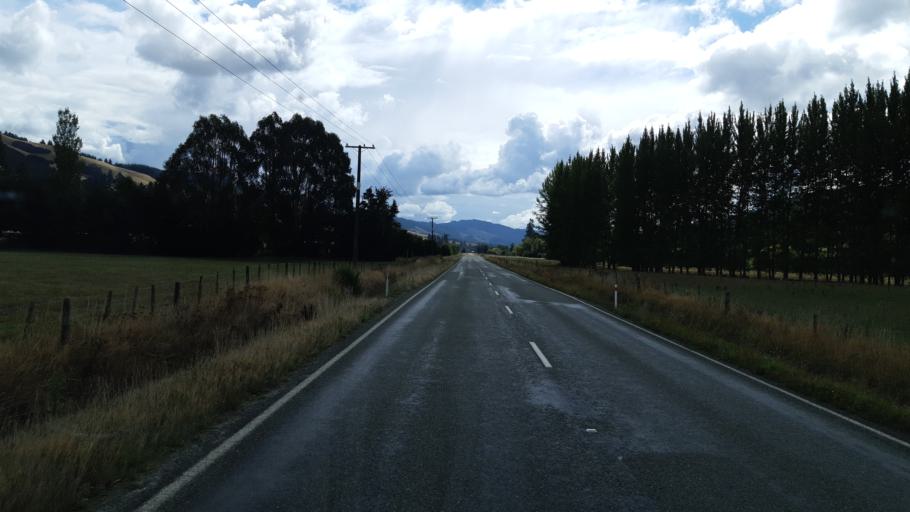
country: NZ
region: Tasman
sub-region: Tasman District
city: Wakefield
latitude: -41.5315
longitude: 172.7959
